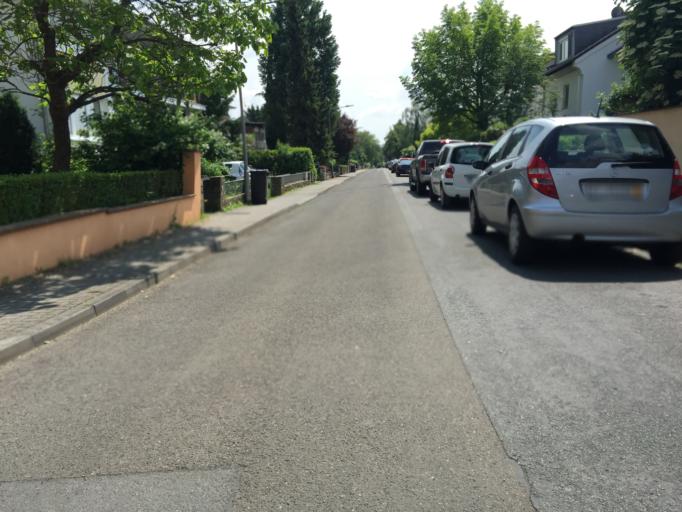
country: DE
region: Hesse
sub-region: Regierungsbezirk Darmstadt
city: Wiesbaden
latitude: 50.0811
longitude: 8.2576
